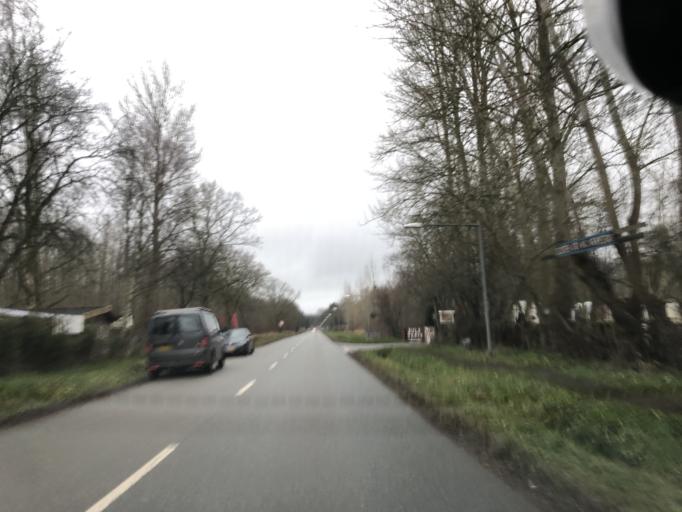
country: DK
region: Capital Region
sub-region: Tarnby Kommune
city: Tarnby
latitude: 55.5849
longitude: 12.5789
